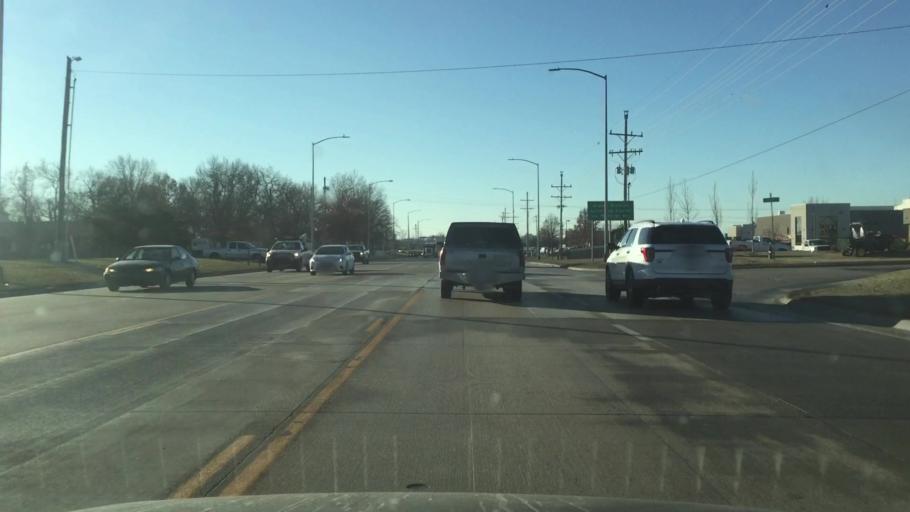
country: US
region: Kansas
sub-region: Johnson County
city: Olathe
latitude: 38.8430
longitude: -94.8160
